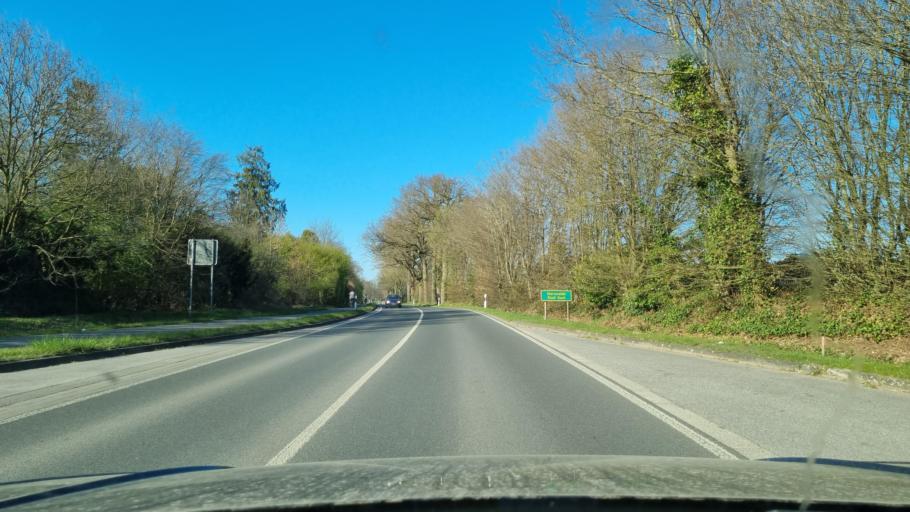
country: DE
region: North Rhine-Westphalia
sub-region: Regierungsbezirk Dusseldorf
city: Goch
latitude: 51.7100
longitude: 6.1287
